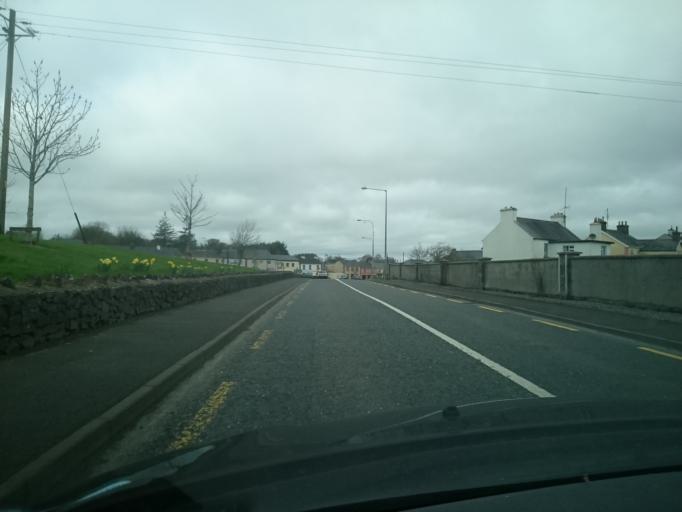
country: IE
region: Connaught
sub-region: Maigh Eo
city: Kiltamagh
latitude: 53.8019
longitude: -9.1268
